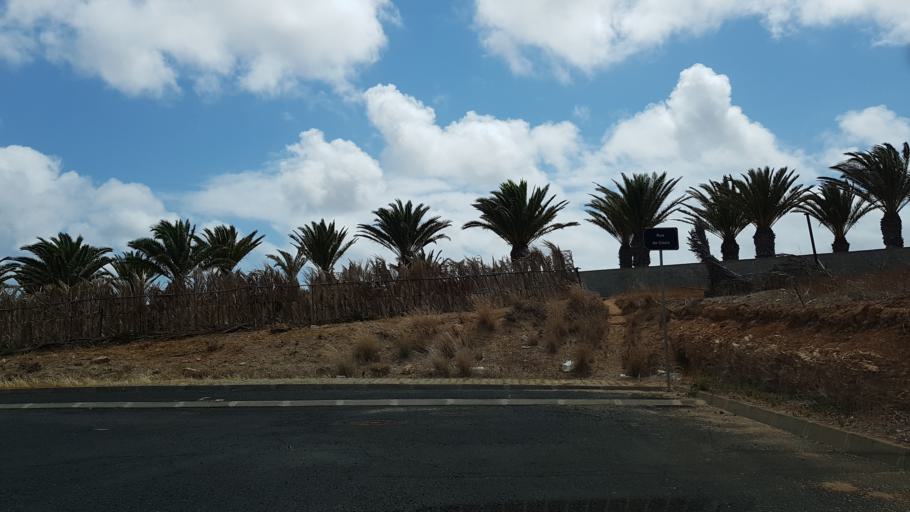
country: PT
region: Madeira
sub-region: Porto Santo
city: Vila de Porto Santo
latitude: 33.0586
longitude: -16.3448
